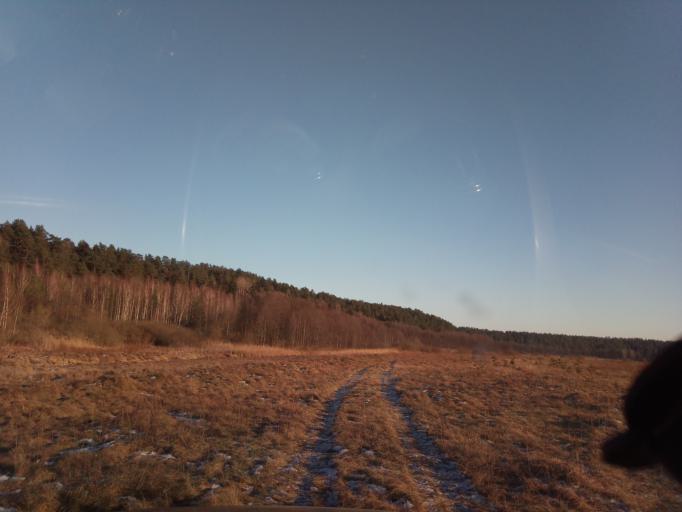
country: LT
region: Alytaus apskritis
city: Druskininkai
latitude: 53.9722
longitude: 23.9664
